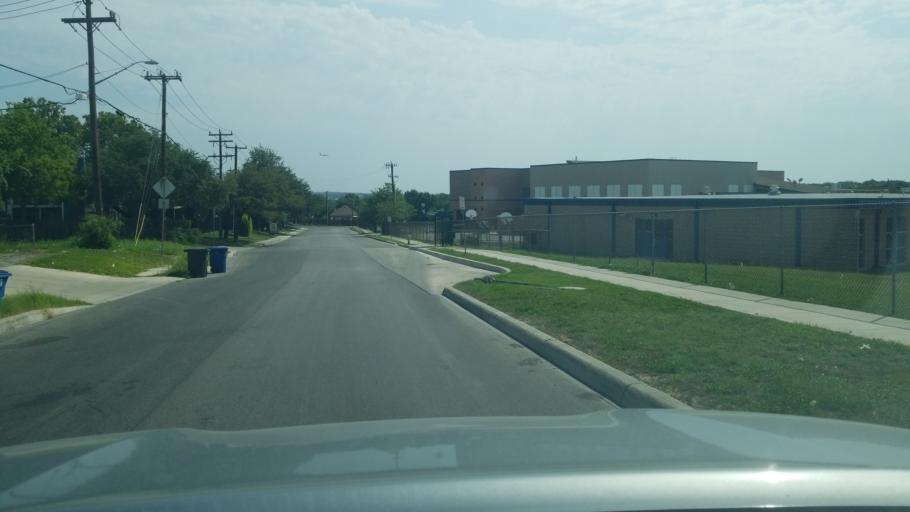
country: US
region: Texas
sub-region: Bexar County
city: Castle Hills
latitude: 29.5431
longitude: -98.5236
